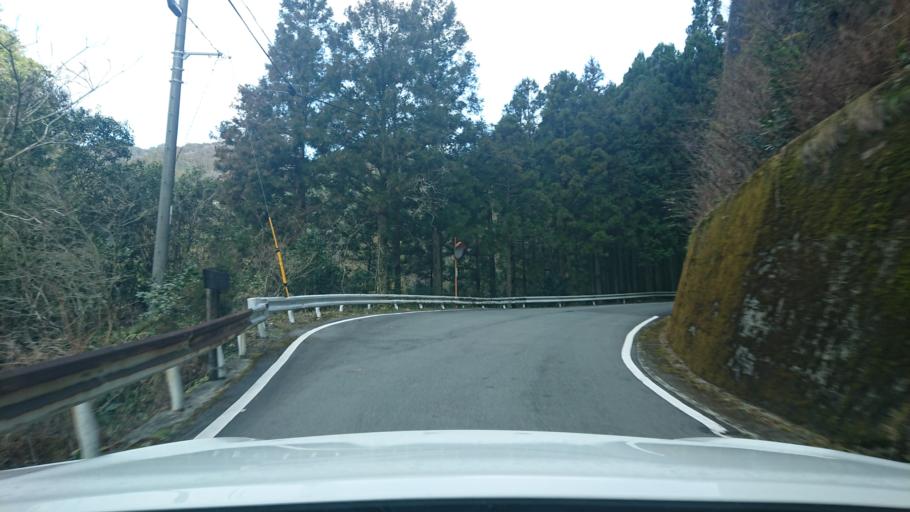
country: JP
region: Tokushima
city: Kamojimacho-jogejima
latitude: 33.9081
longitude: 134.3941
